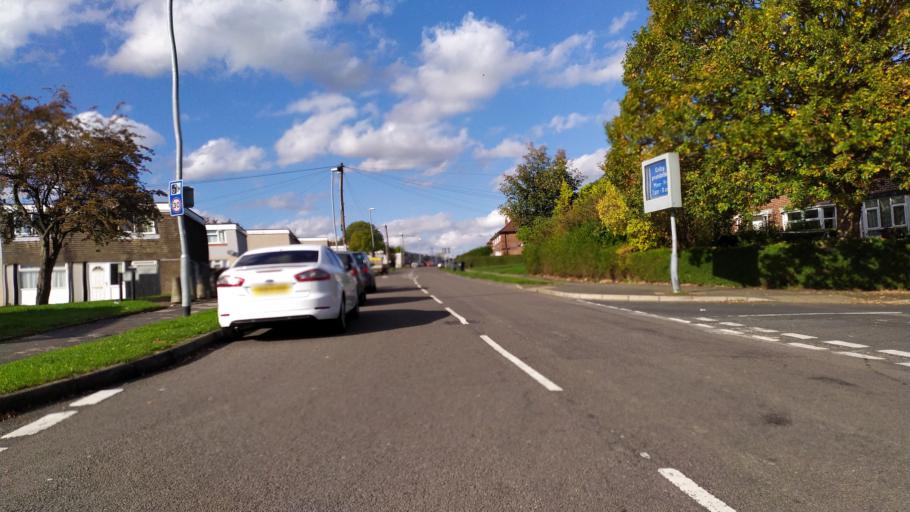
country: GB
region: England
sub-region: City and Borough of Leeds
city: Horsforth
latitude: 53.8225
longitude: -1.5990
